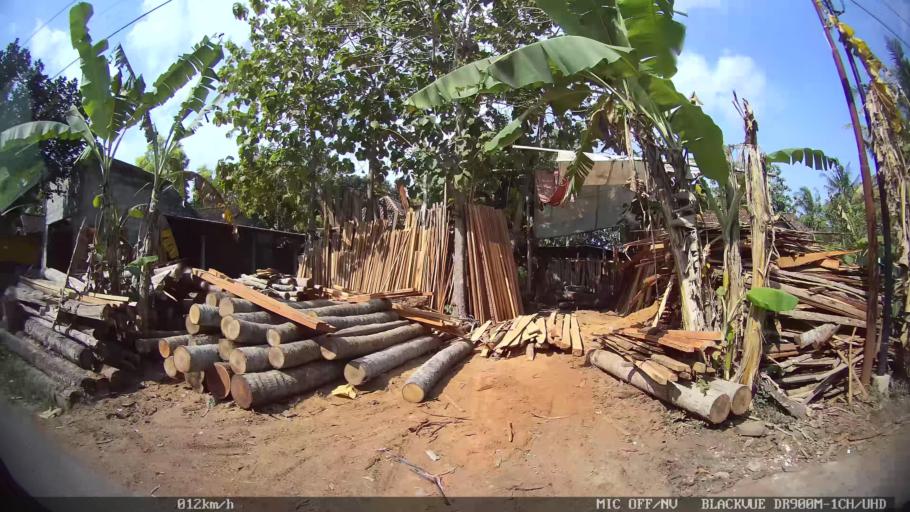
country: ID
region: Daerah Istimewa Yogyakarta
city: Kasihan
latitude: -7.8508
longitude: 110.2999
